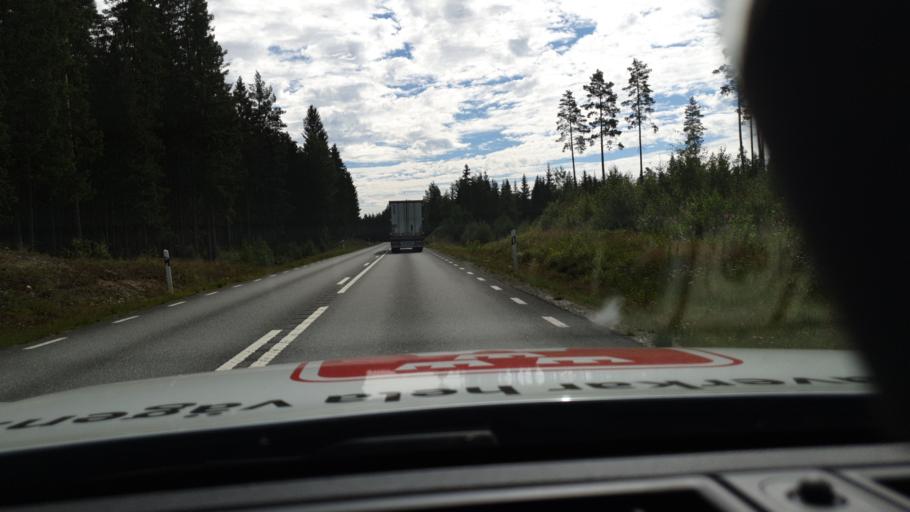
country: SE
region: Joenkoeping
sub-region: Savsjo Kommun
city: Vrigstad
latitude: 57.3724
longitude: 14.4154
